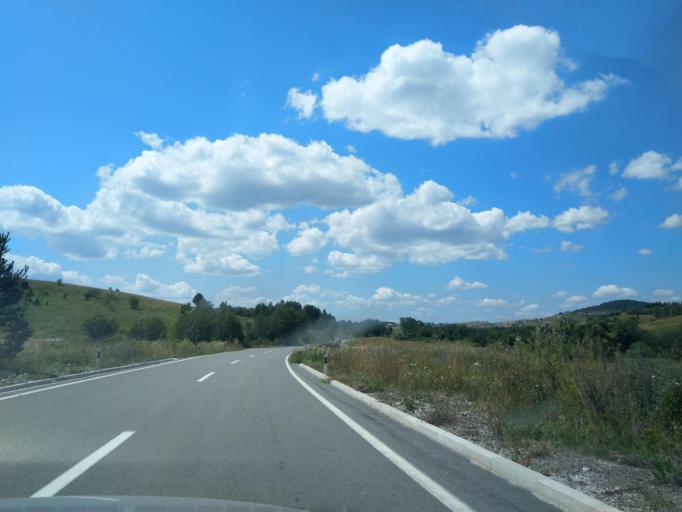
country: RS
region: Central Serbia
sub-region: Zlatiborski Okrug
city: Sjenica
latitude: 43.3275
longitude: 19.8868
